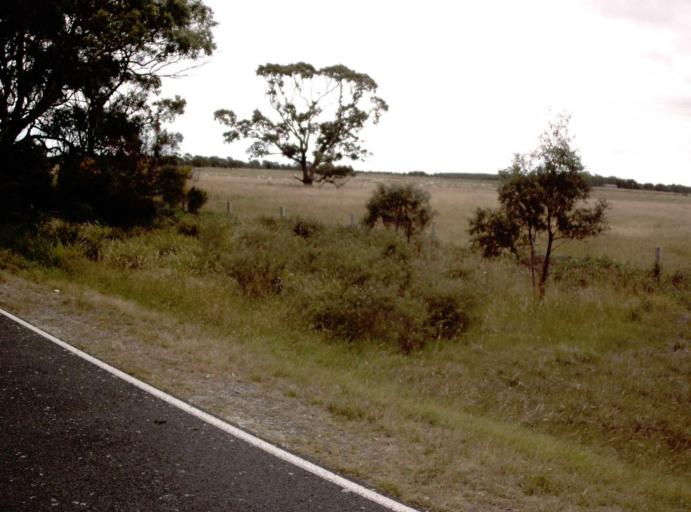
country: AU
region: Victoria
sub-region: Wellington
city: Sale
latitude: -38.5797
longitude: 146.8762
